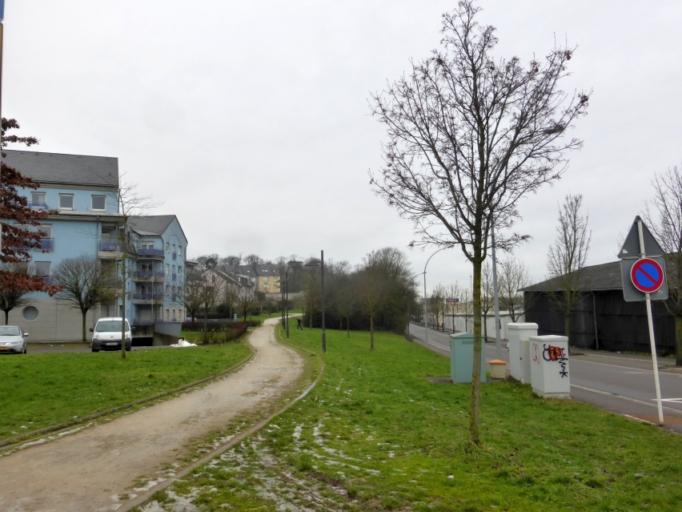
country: LU
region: Luxembourg
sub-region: Canton de Luxembourg
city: Luxembourg
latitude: 49.5942
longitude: 6.1259
